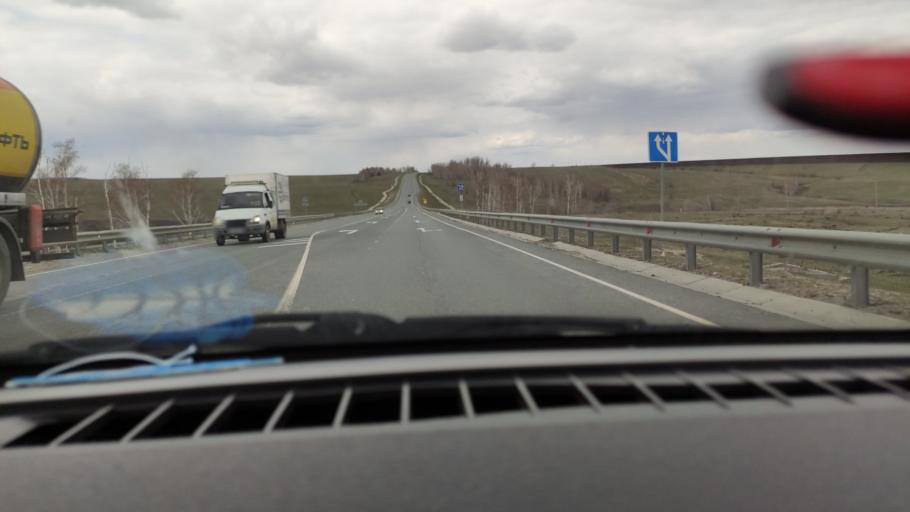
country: RU
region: Saratov
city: Shikhany
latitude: 52.1194
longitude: 47.2684
